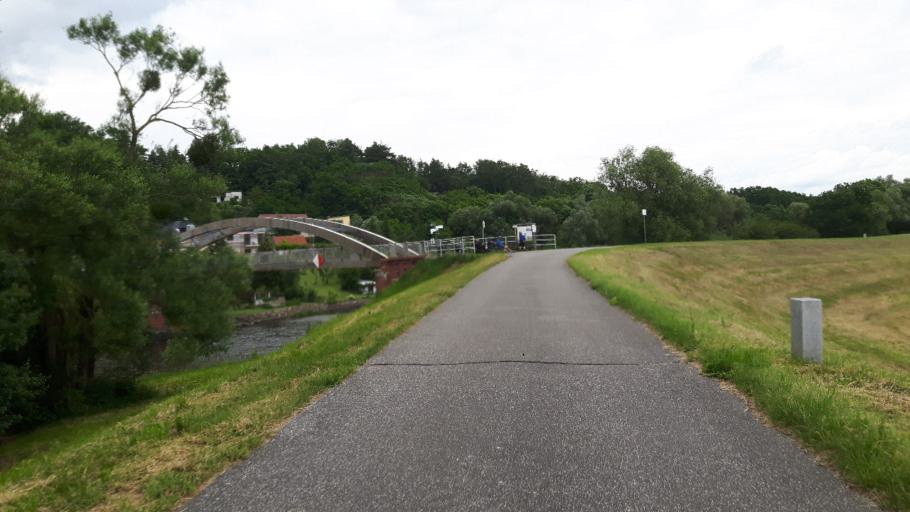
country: DE
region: Brandenburg
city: Schoneberg
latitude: 52.9917
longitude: 14.1756
